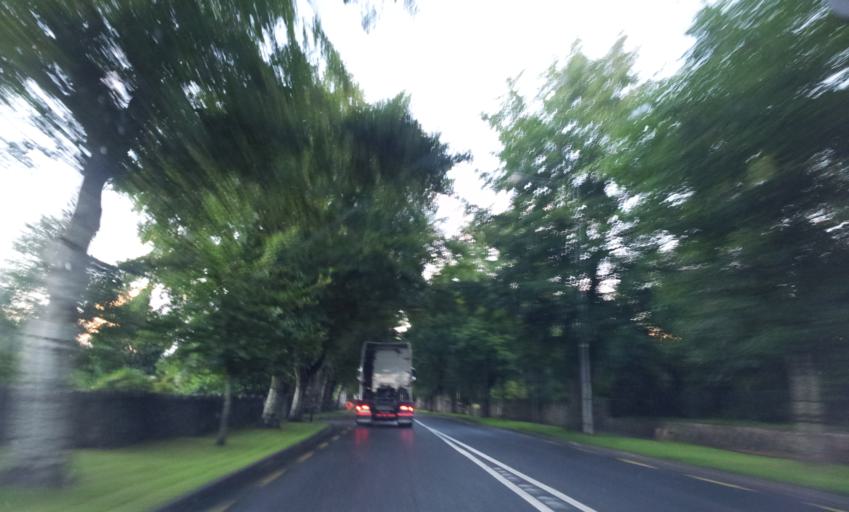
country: IE
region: Munster
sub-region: County Limerick
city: Adare
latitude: 52.5582
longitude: -8.7960
